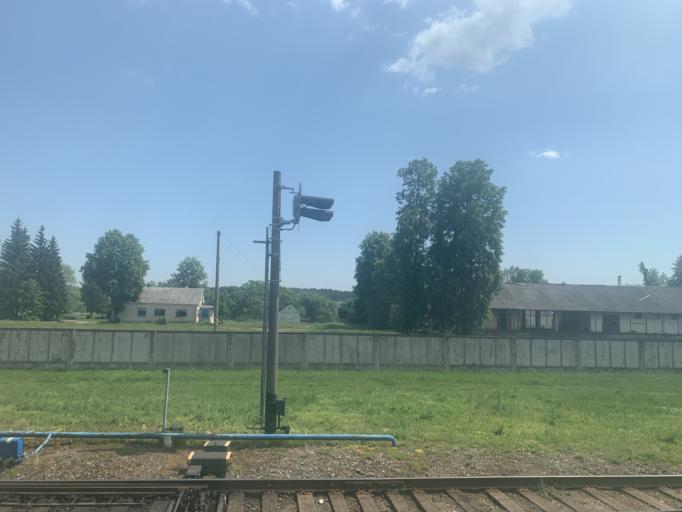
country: BY
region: Minsk
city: Stowbtsy
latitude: 53.4874
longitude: 26.7634
